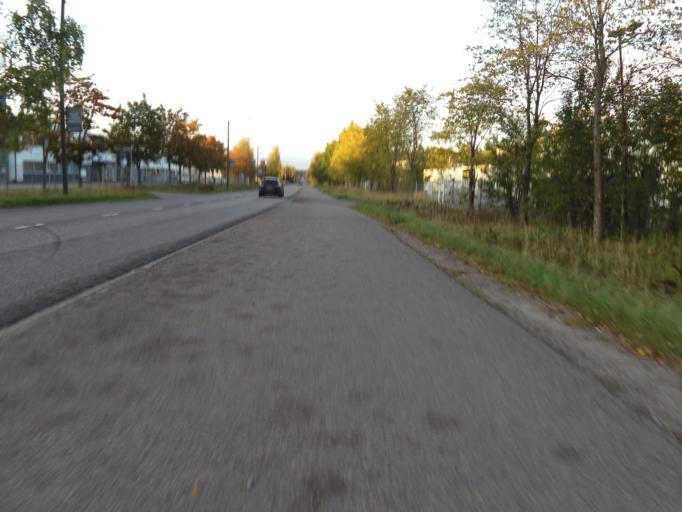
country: FI
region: Uusimaa
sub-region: Helsinki
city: Kilo
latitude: 60.2727
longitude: 24.7606
